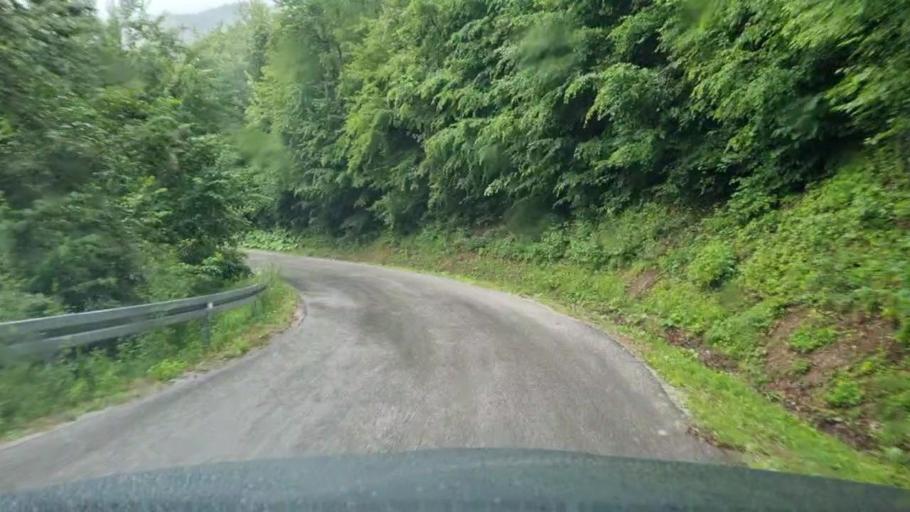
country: BA
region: Federation of Bosnia and Herzegovina
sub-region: Bosansko-Podrinjski Kanton
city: Ustikolina
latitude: 43.6352
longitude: 18.6273
